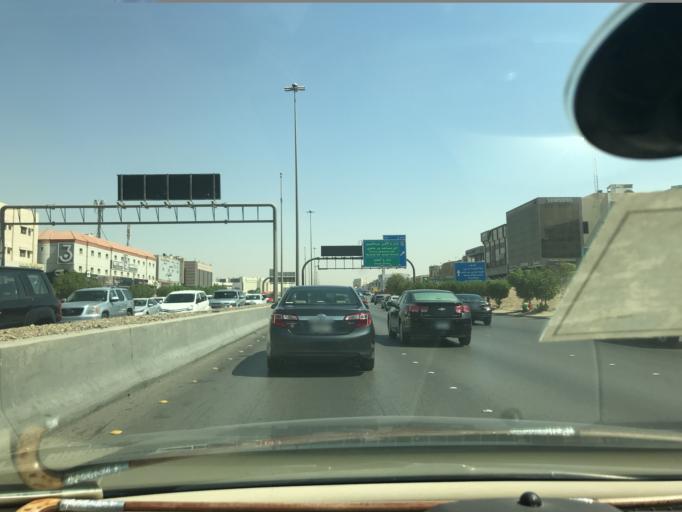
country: SA
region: Ar Riyad
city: Riyadh
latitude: 24.6811
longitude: 46.6944
